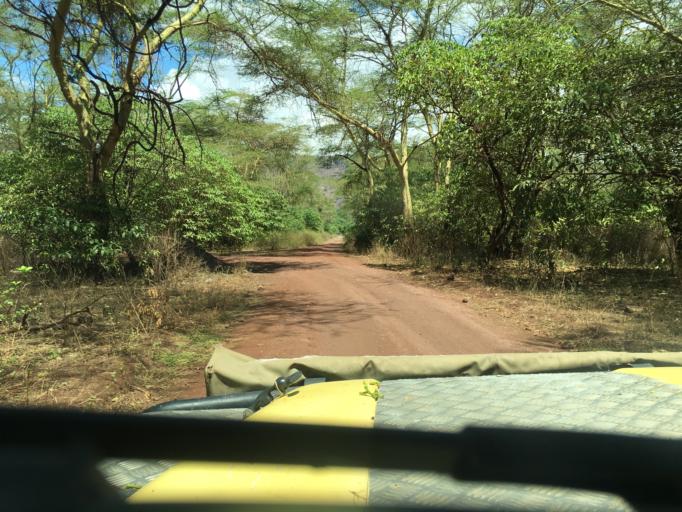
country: TZ
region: Arusha
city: Mto wa Mbu
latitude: -3.4062
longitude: 35.8256
